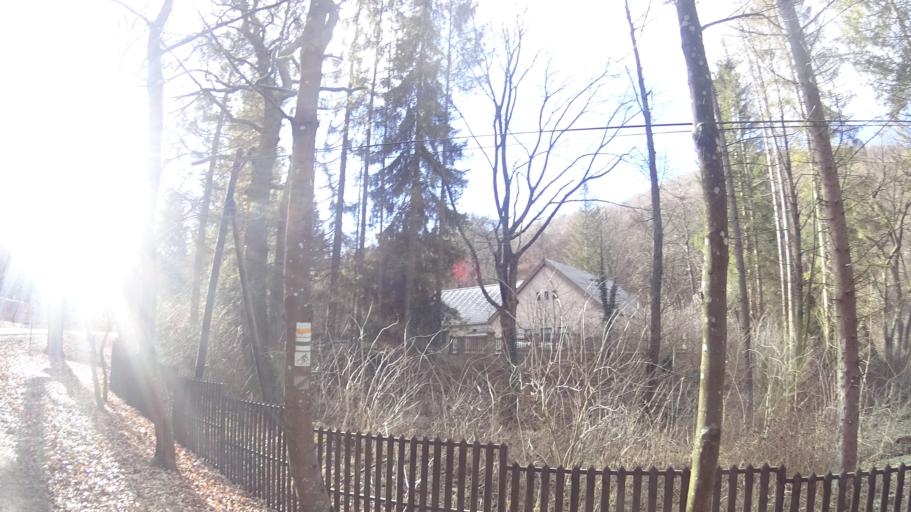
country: HU
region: Heves
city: Szilvasvarad
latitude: 48.0865
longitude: 20.4067
